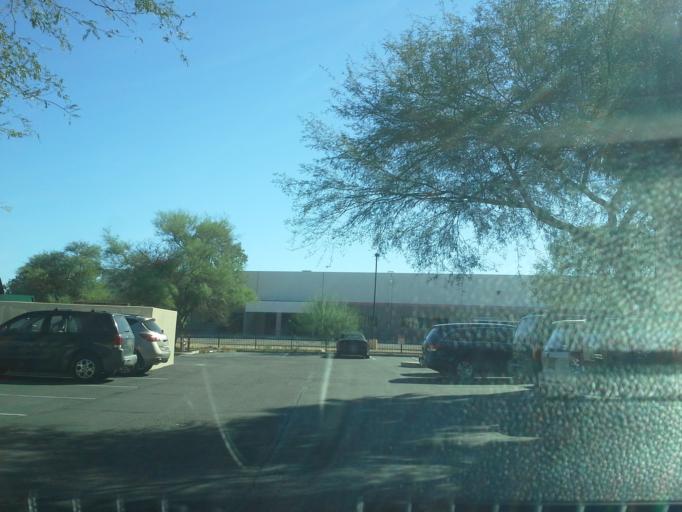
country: US
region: Arizona
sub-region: Pima County
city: Summit
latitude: 32.1261
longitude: -110.9331
